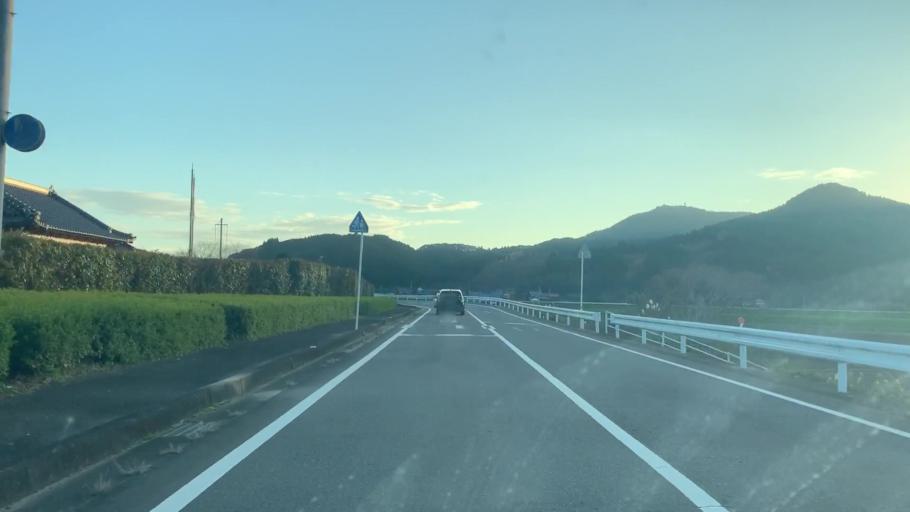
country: JP
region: Saga Prefecture
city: Imaricho-ko
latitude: 33.3049
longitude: 129.9682
